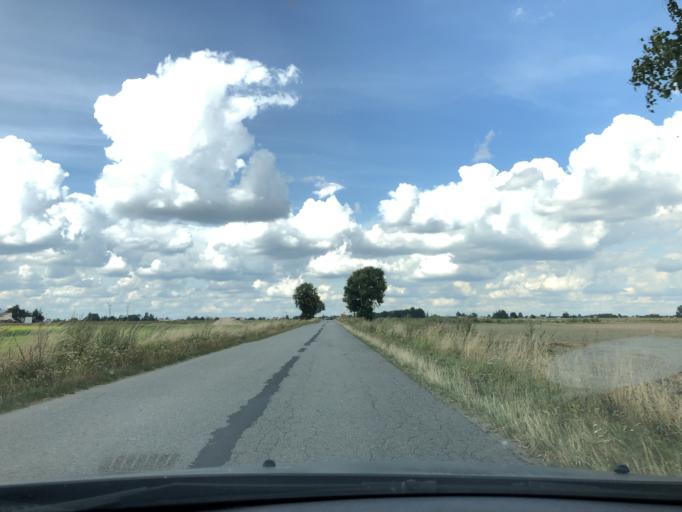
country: PL
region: Lodz Voivodeship
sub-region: Powiat wieruszowski
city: Walichnowy
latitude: 51.2507
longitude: 18.3898
